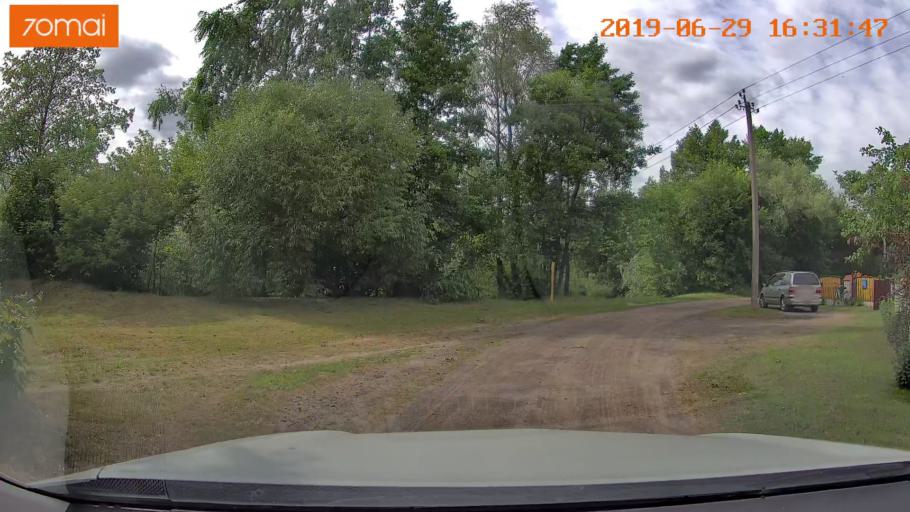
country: BY
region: Brest
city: Luninyets
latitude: 52.2005
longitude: 27.0104
